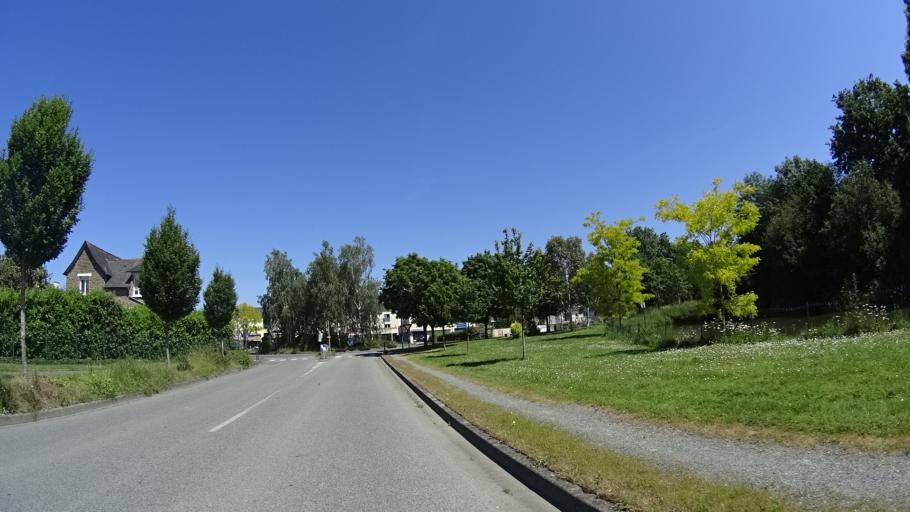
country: FR
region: Brittany
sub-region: Departement d'Ille-et-Vilaine
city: Messac
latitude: 47.8230
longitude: -1.8099
